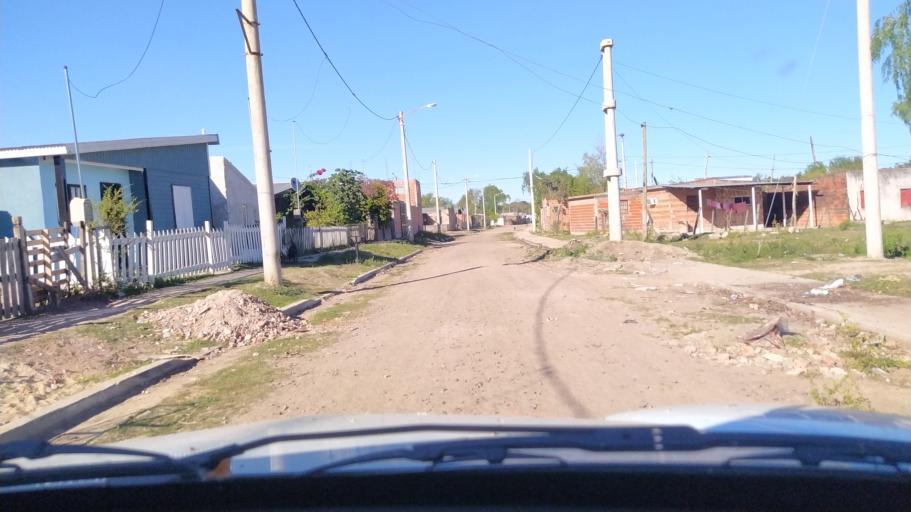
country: AR
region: Corrientes
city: Corrientes
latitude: -27.4950
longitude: -58.8081
